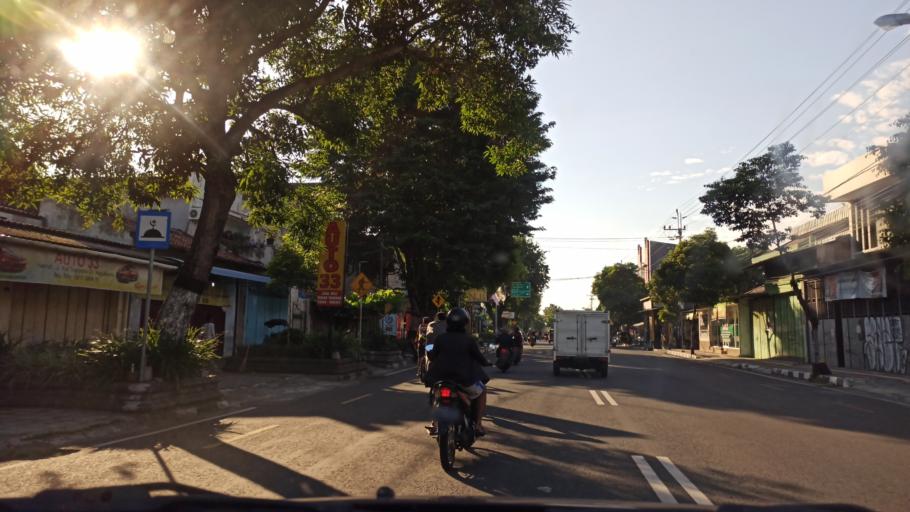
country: ID
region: Daerah Istimewa Yogyakarta
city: Yogyakarta
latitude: -7.8145
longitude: 110.3714
